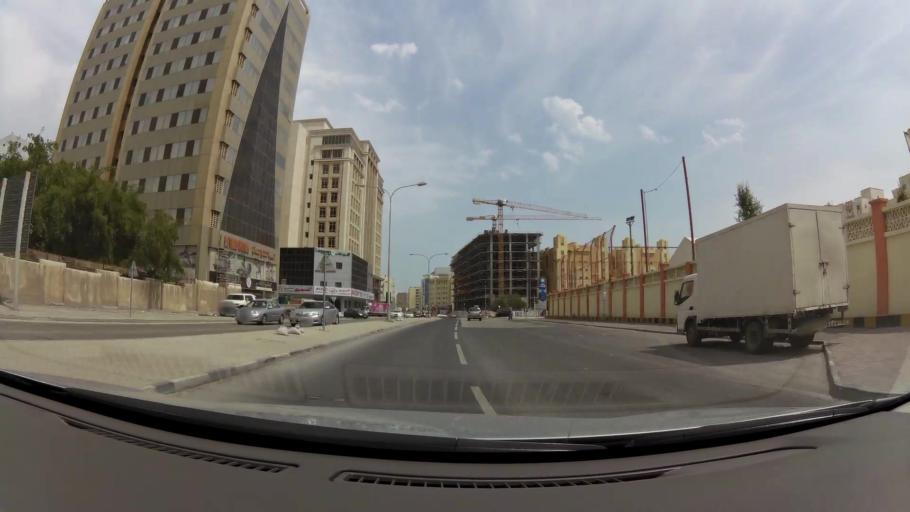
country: QA
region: Baladiyat ad Dawhah
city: Doha
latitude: 25.2748
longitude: 51.5294
